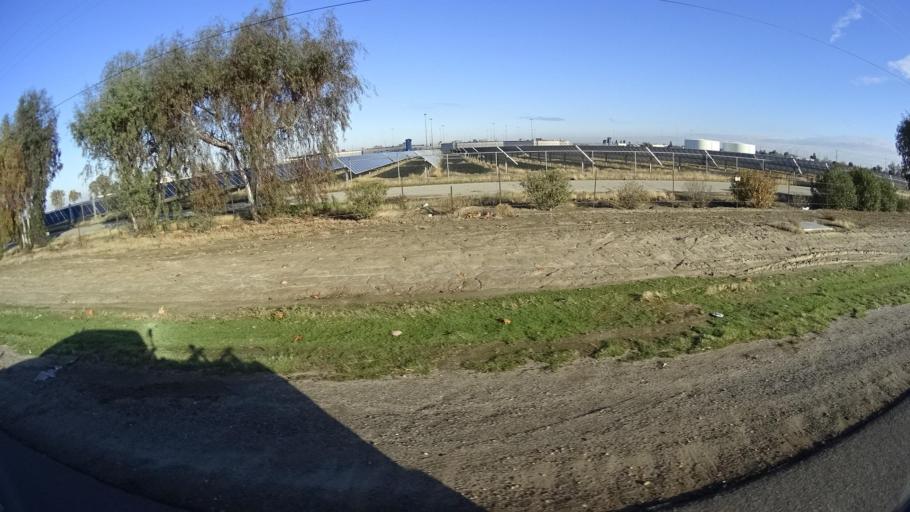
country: US
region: California
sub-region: Kern County
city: Delano
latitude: 35.7759
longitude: -119.3090
